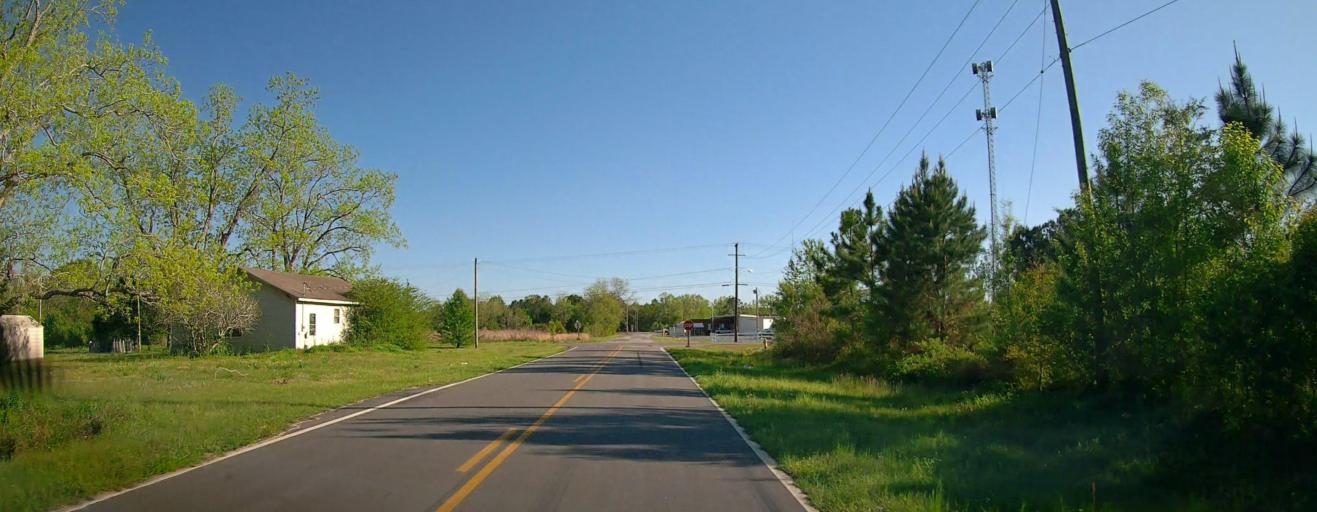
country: US
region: Georgia
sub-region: Ben Hill County
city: Fitzgerald
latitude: 31.7293
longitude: -83.2801
